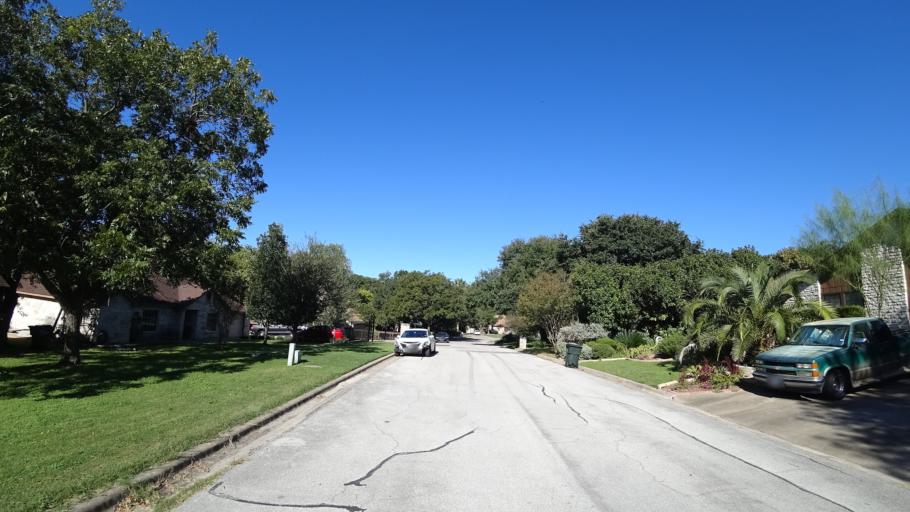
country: US
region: Texas
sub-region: Travis County
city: Manor
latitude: 30.3327
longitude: -97.6536
